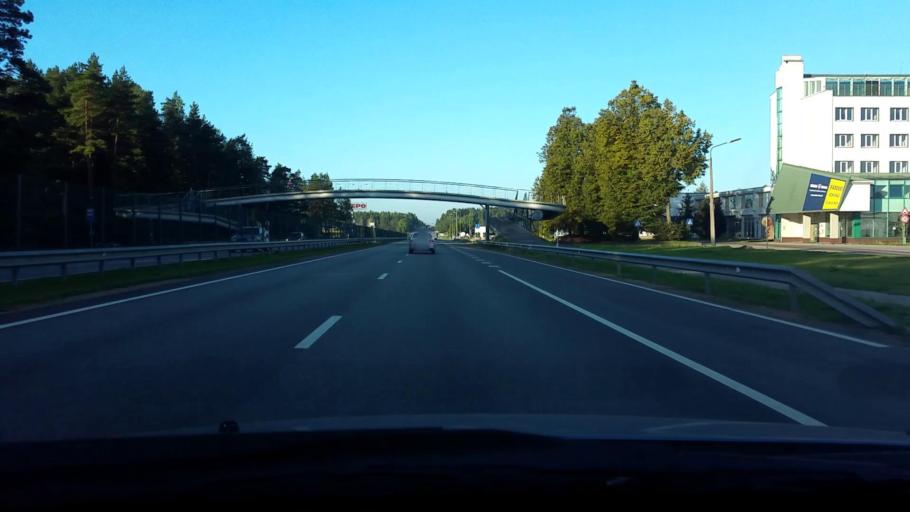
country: LV
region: Riga
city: Bergi
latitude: 57.0050
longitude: 24.2920
